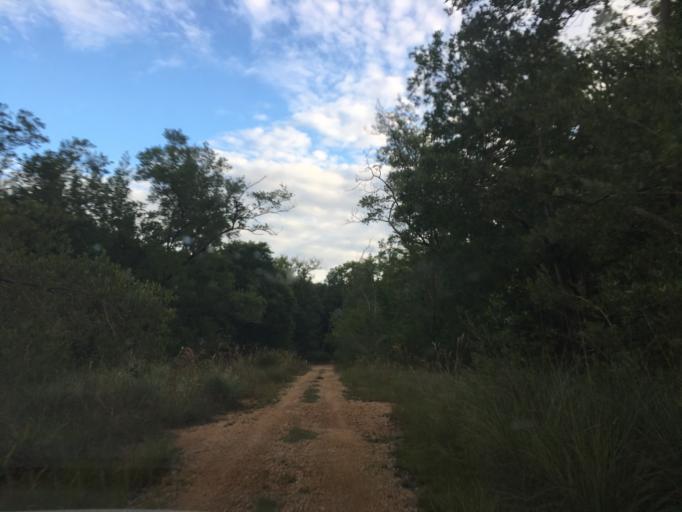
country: BZ
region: Stann Creek
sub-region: Dangriga
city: Dangriga
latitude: 16.8104
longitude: -88.2555
